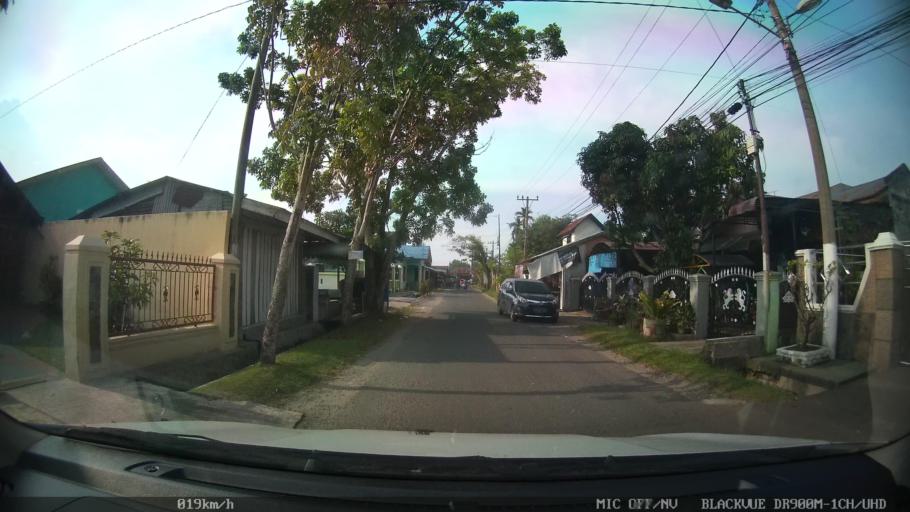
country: ID
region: North Sumatra
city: Binjai
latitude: 3.6075
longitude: 98.5112
